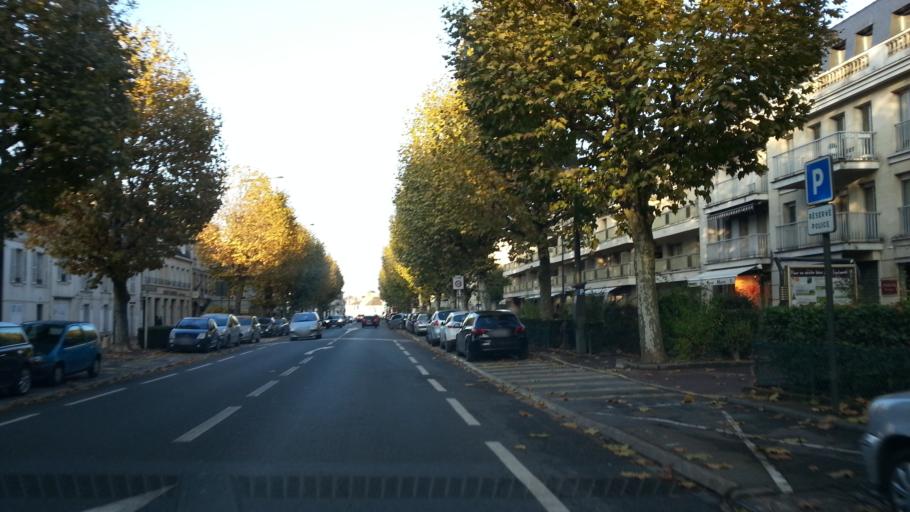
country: FR
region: Picardie
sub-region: Departement de l'Oise
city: Chantilly
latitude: 49.1917
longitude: 2.4642
